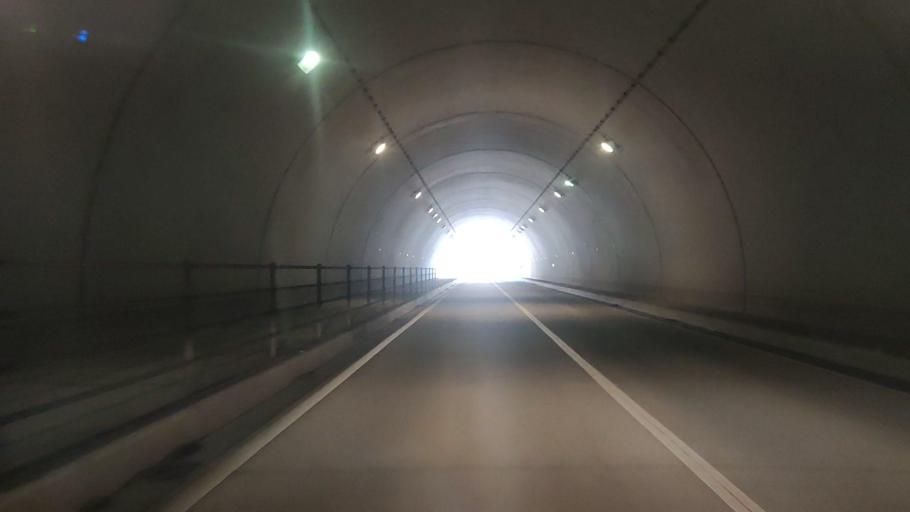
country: JP
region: Oita
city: Saiki
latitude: 32.8049
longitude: 131.8976
